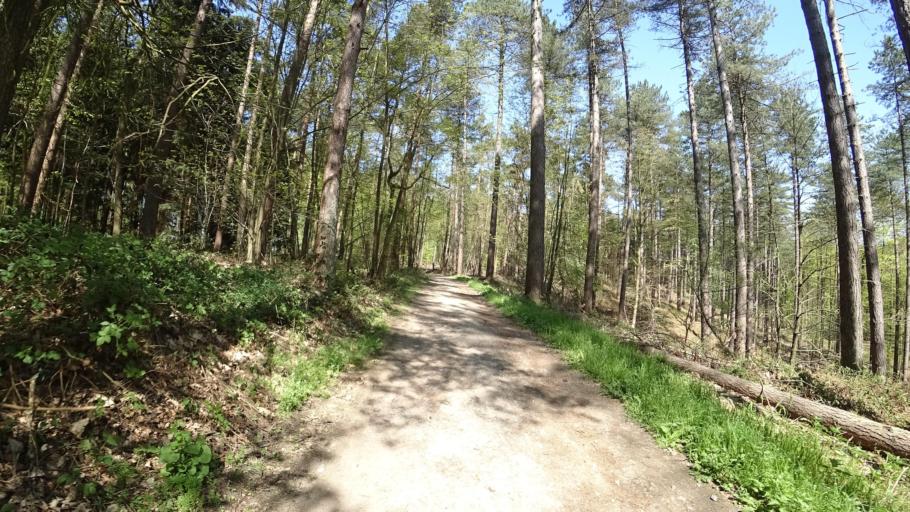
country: BE
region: Wallonia
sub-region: Province du Brabant Wallon
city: Braine-le-Chateau
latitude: 50.7083
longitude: 4.2992
